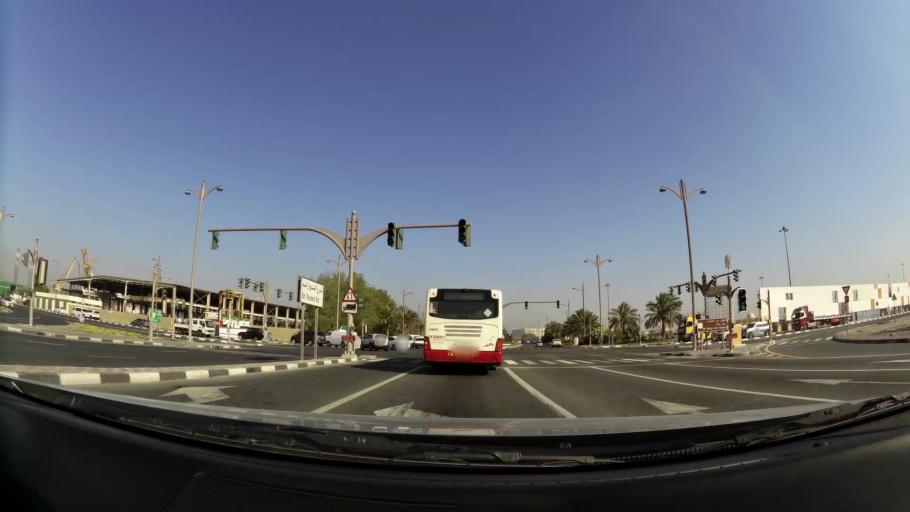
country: AE
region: Ash Shariqah
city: Sharjah
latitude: 25.2508
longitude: 55.2788
